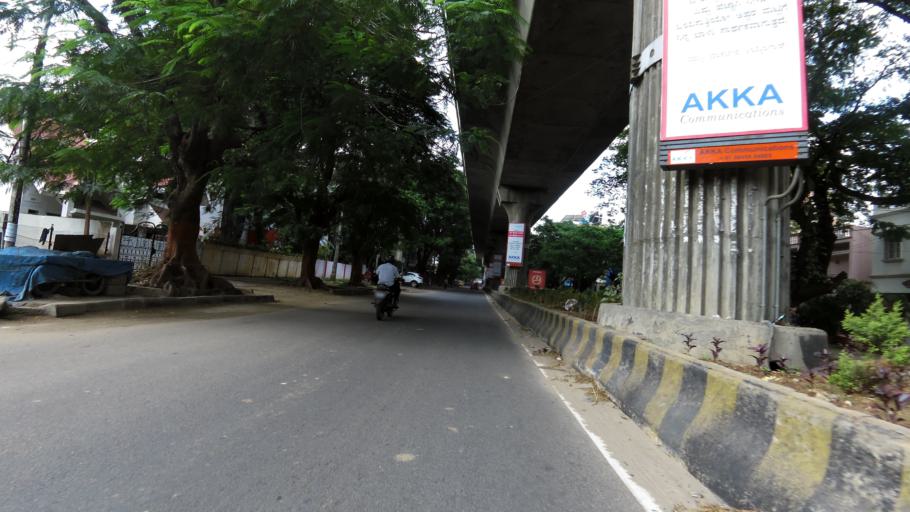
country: IN
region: Karnataka
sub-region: Bangalore Urban
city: Bangalore
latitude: 12.9841
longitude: 77.6408
